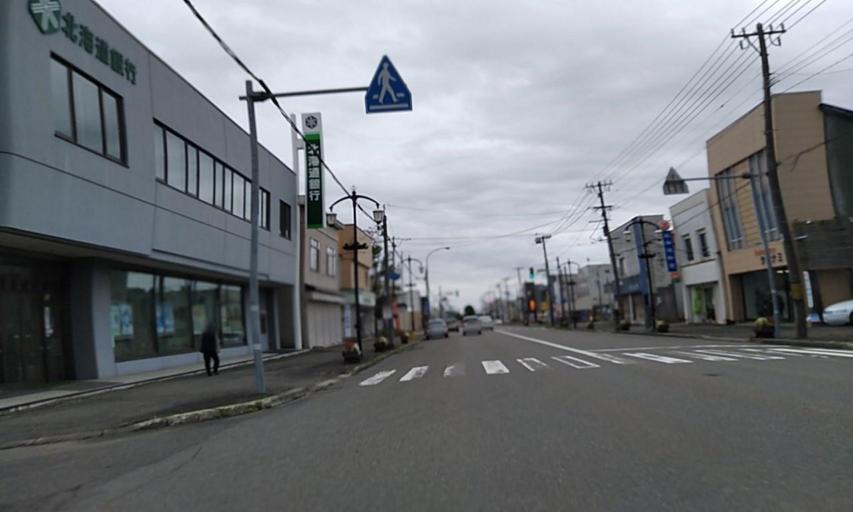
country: JP
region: Hokkaido
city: Obihiro
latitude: 42.2881
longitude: 143.3160
